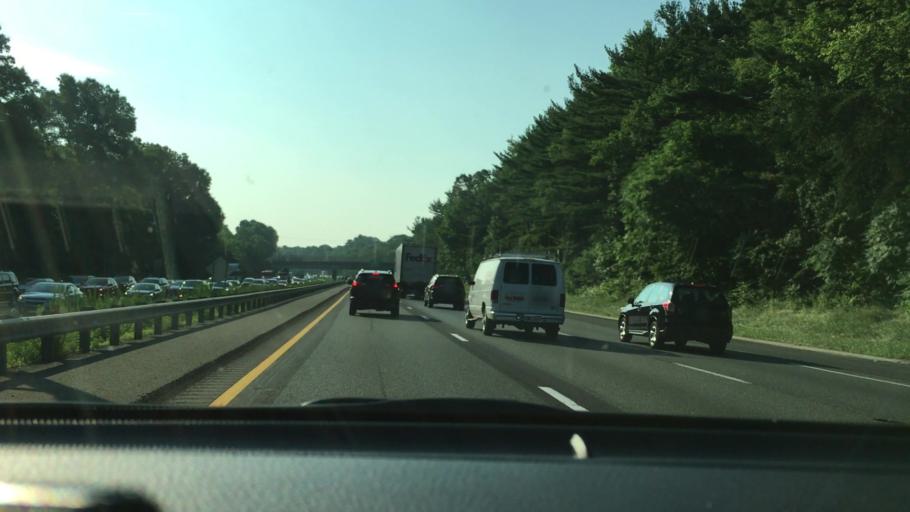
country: US
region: New Jersey
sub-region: Camden County
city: Lawnside
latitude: 39.8736
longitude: -75.0410
